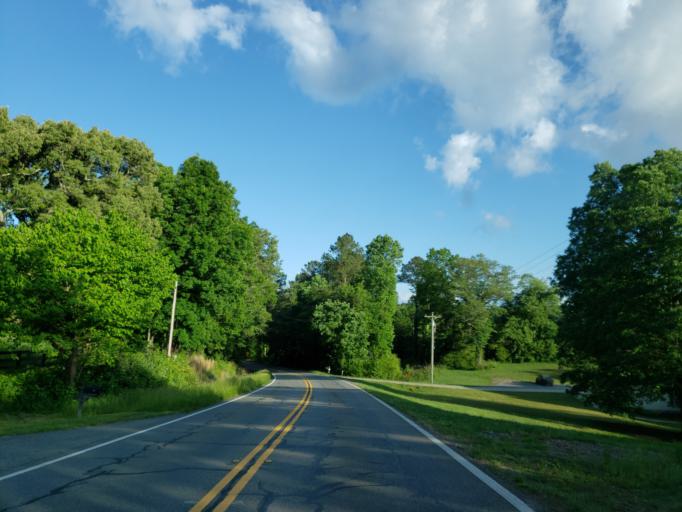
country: US
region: Georgia
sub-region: Cherokee County
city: Canton
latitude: 34.3422
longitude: -84.5771
